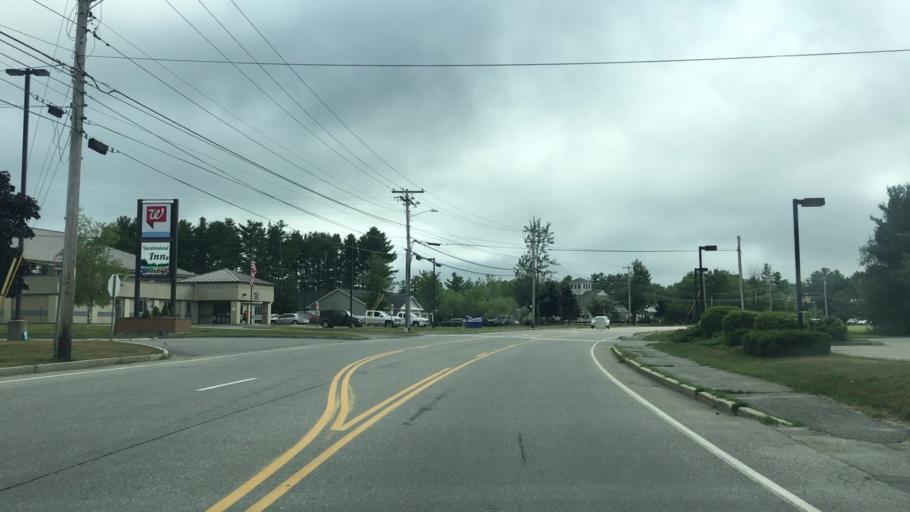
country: US
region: Maine
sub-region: Penobscot County
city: Brewer
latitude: 44.7830
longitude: -68.7510
